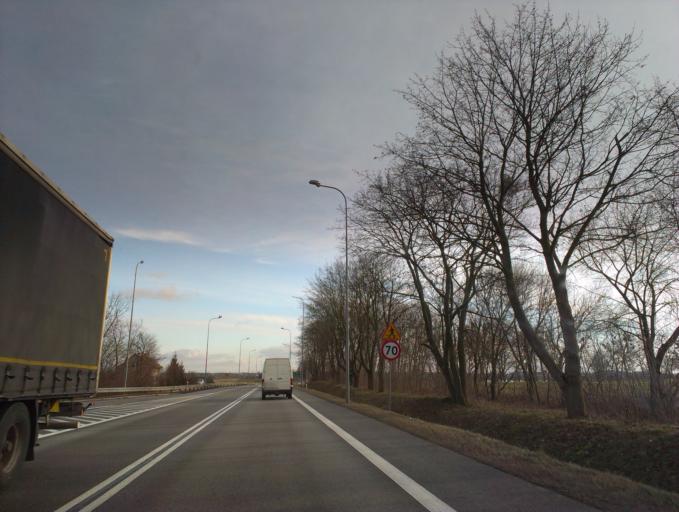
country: PL
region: Kujawsko-Pomorskie
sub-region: Powiat lipnowski
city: Kikol
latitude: 52.9273
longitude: 19.0813
